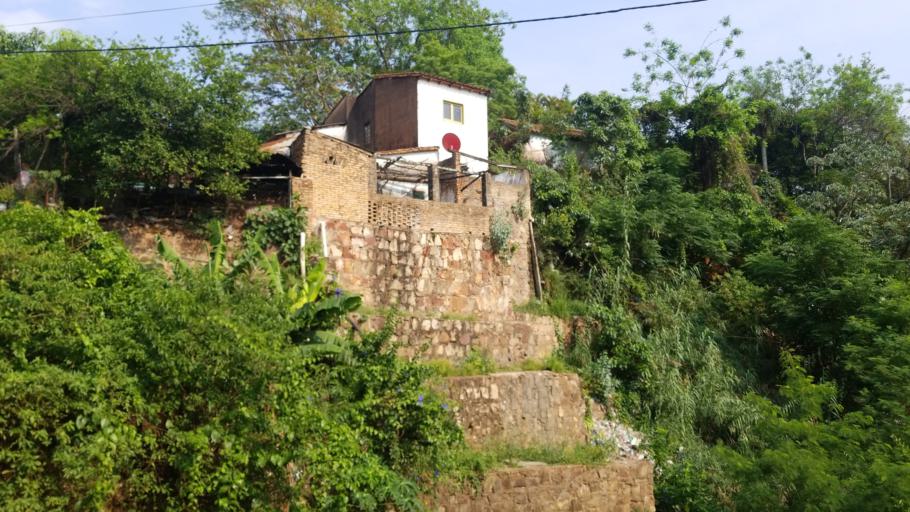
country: PY
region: Asuncion
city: Asuncion
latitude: -25.2821
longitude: -57.6265
